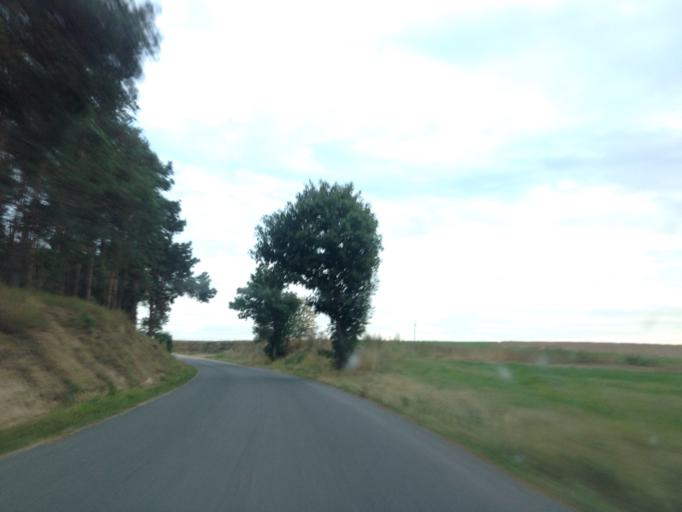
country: PL
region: Kujawsko-Pomorskie
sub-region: Powiat brodnicki
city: Brzozie
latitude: 53.2941
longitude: 19.6901
